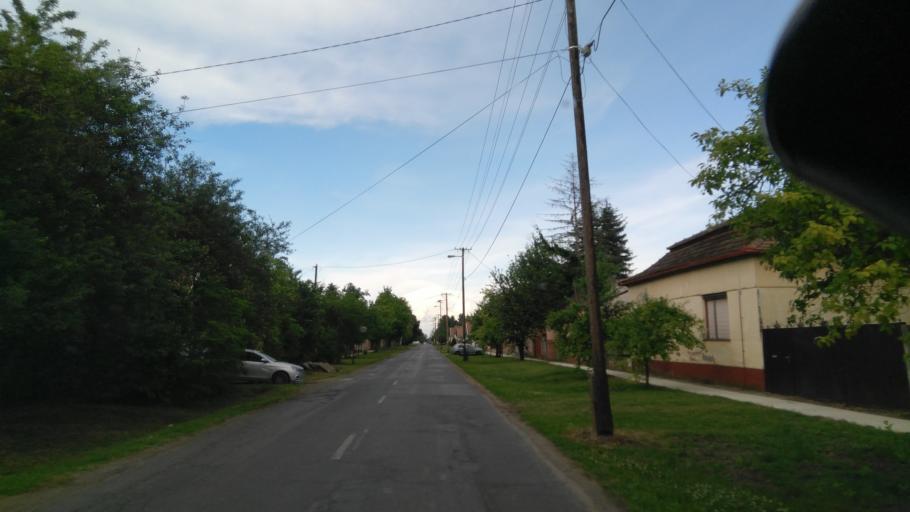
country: HU
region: Bekes
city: Kevermes
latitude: 46.4130
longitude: 21.1757
